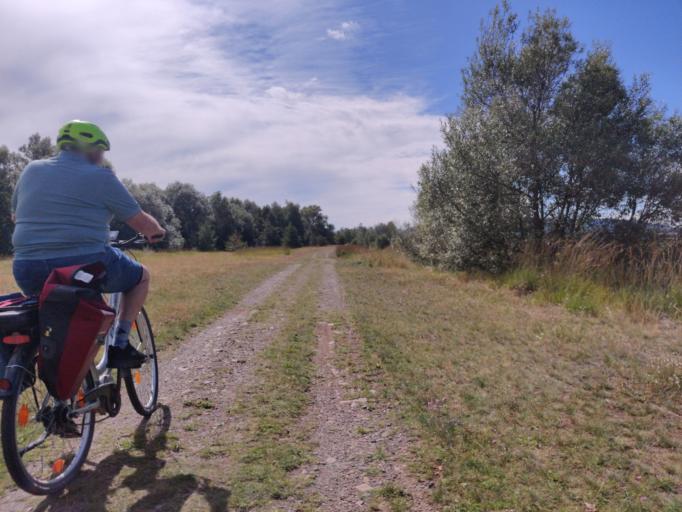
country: DE
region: Lower Saxony
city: Langelsheim
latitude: 51.9712
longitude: 10.3693
